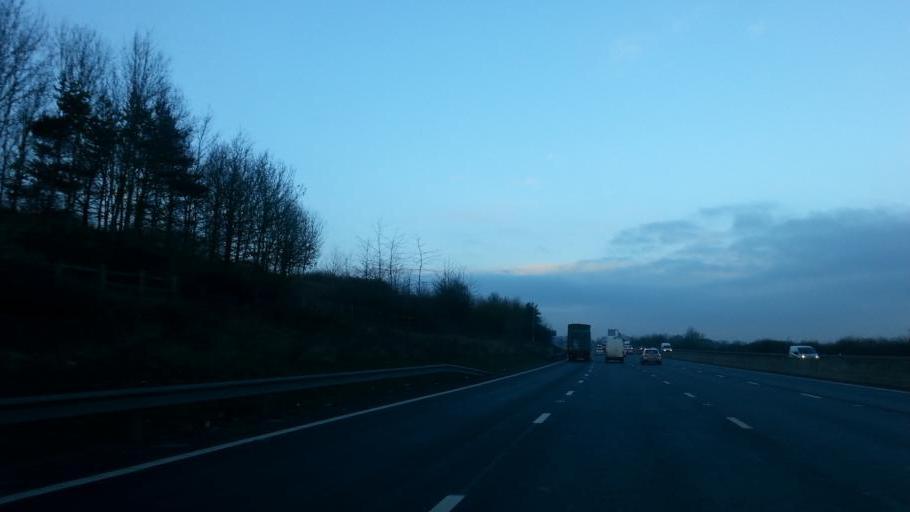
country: GB
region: England
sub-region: Worcestershire
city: Droitwich
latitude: 52.2388
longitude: -2.1356
